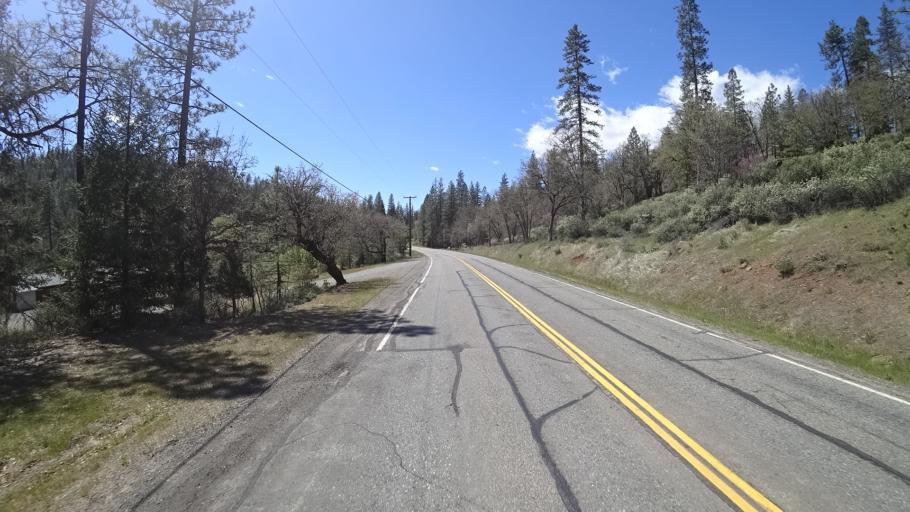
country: US
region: California
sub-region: Trinity County
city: Weaverville
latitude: 40.7511
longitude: -122.8949
